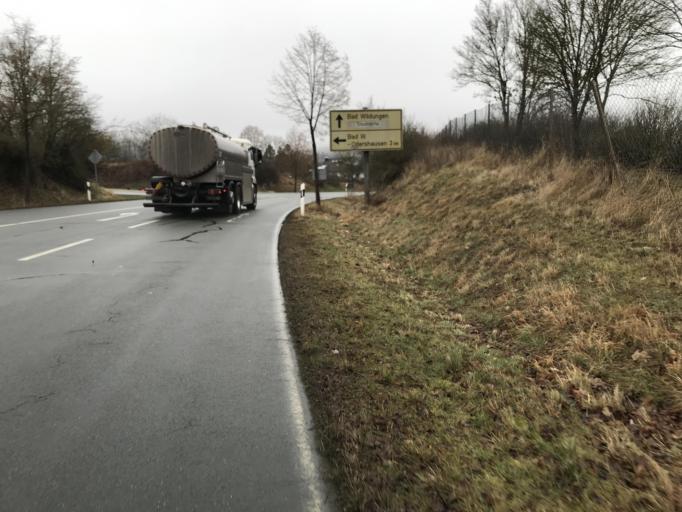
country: DE
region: Hesse
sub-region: Regierungsbezirk Kassel
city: Bad Wildungen
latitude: 51.1059
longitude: 9.1198
